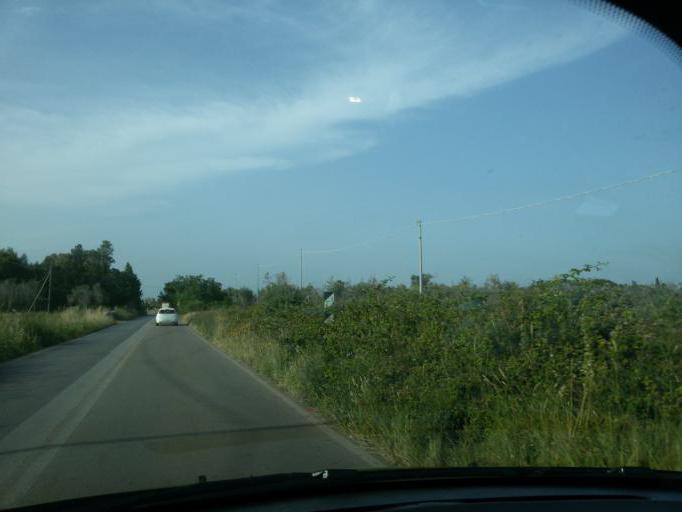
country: IT
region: Apulia
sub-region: Provincia di Lecce
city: Porto Cesareo
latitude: 40.3056
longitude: 17.8616
